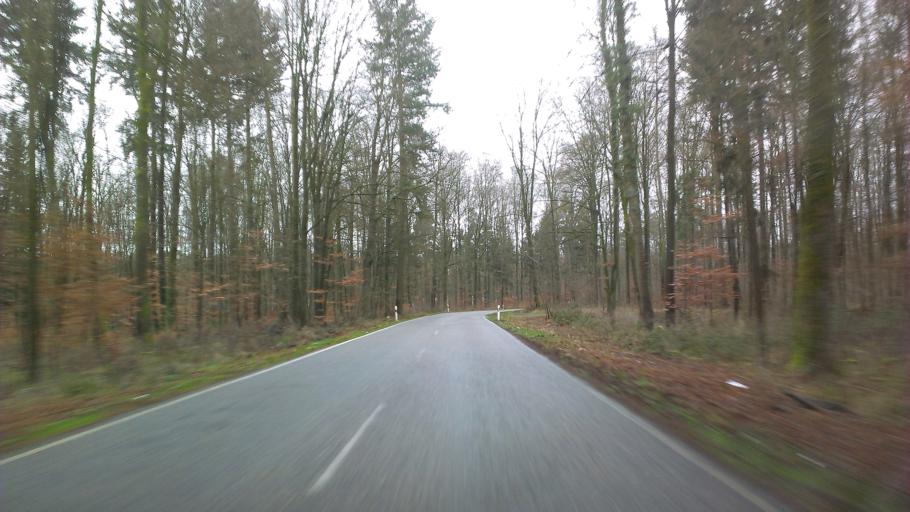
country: DE
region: Baden-Wuerttemberg
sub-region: Regierungsbezirk Stuttgart
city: Zaberfeld
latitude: 49.0893
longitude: 8.9047
